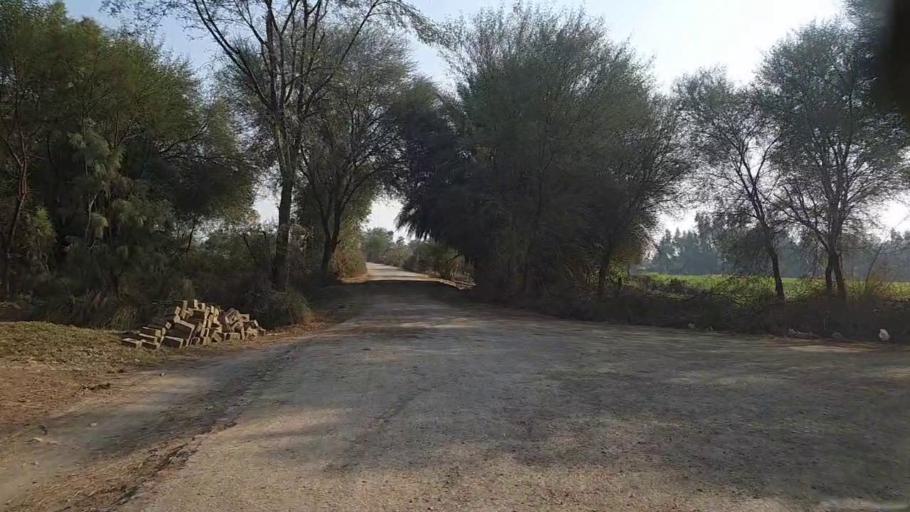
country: PK
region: Sindh
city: Mirpur Mathelo
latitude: 27.8836
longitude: 69.6116
